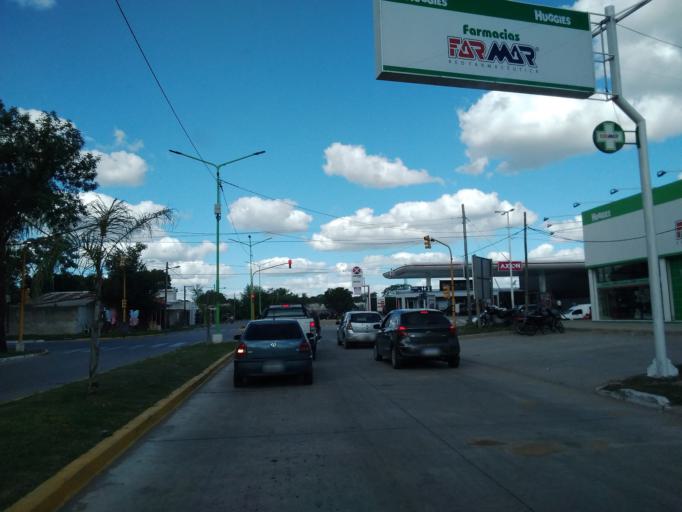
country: AR
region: Corrientes
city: Corrientes
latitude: -27.4994
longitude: -58.8261
